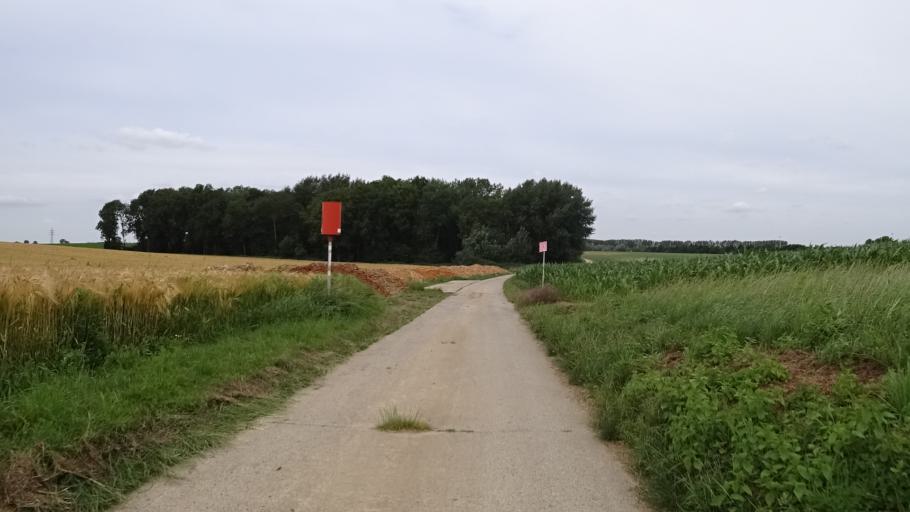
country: BE
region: Wallonia
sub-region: Province du Brabant Wallon
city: Walhain-Saint-Paul
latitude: 50.6556
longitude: 4.6607
